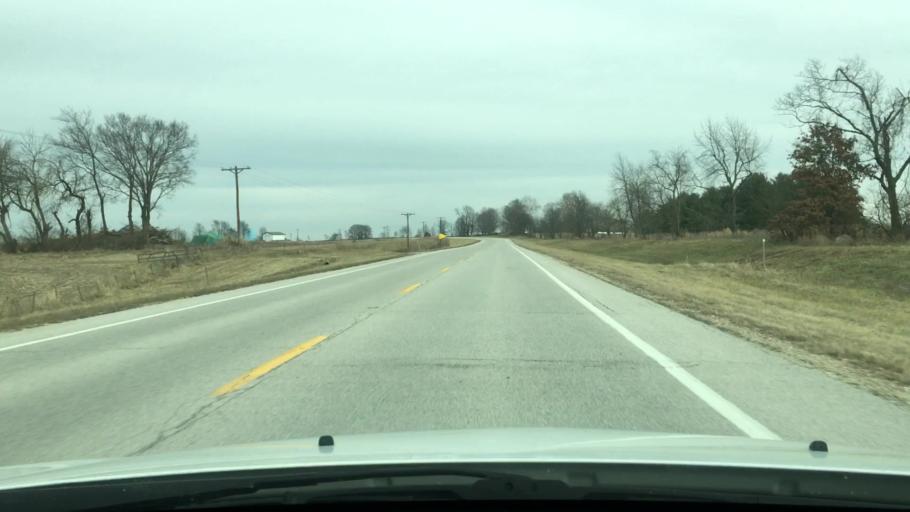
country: US
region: Illinois
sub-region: Pike County
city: Pittsfield
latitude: 39.5291
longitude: -90.9267
